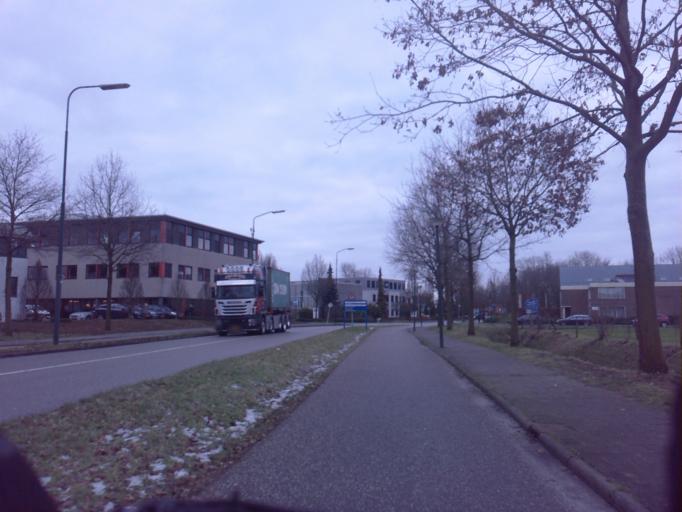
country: NL
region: Utrecht
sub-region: Gemeente Leusden
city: Leusden
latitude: 52.1418
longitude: 5.4250
